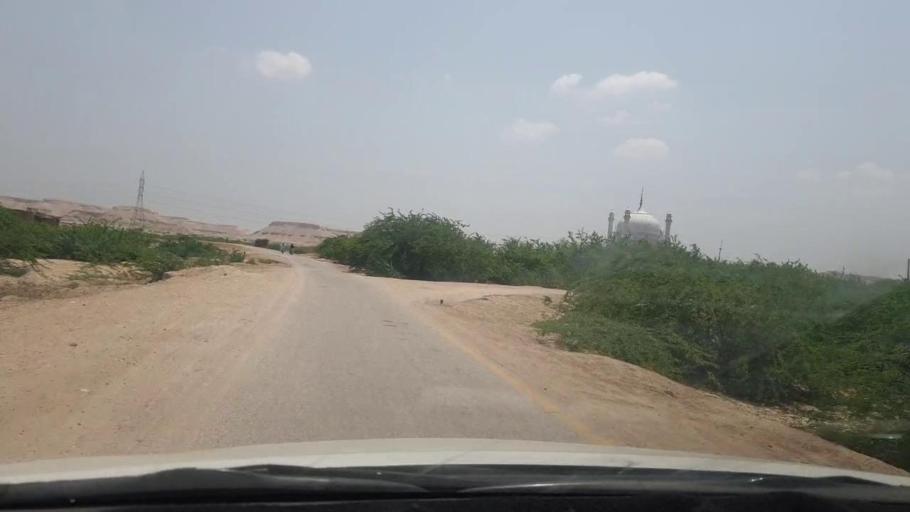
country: PK
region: Sindh
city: Khairpur
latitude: 27.5293
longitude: 68.9039
